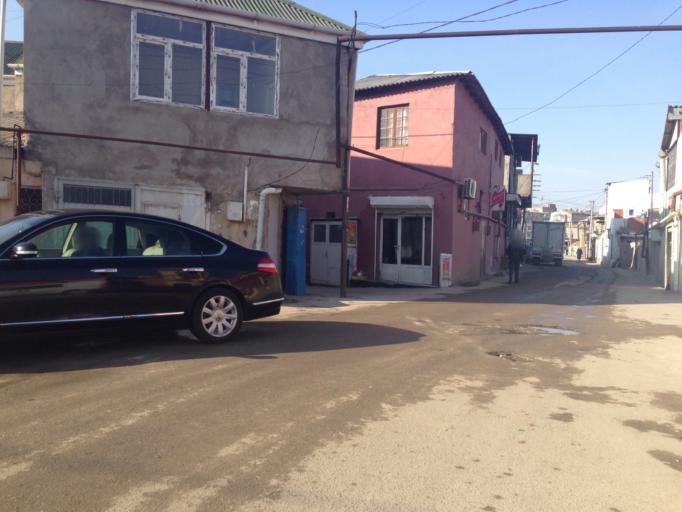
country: AZ
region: Baki
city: Baku
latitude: 40.3965
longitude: 49.8835
